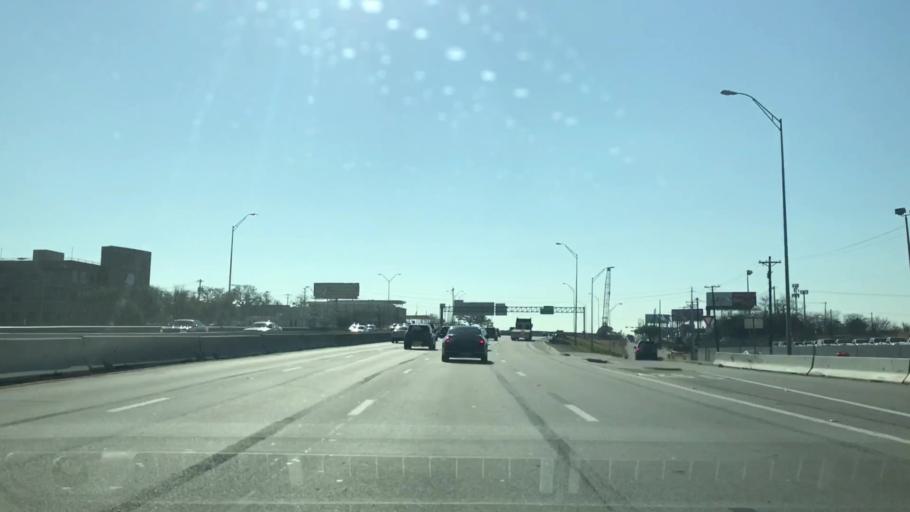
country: US
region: Texas
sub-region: Dallas County
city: Dallas
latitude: 32.7556
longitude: -96.8097
